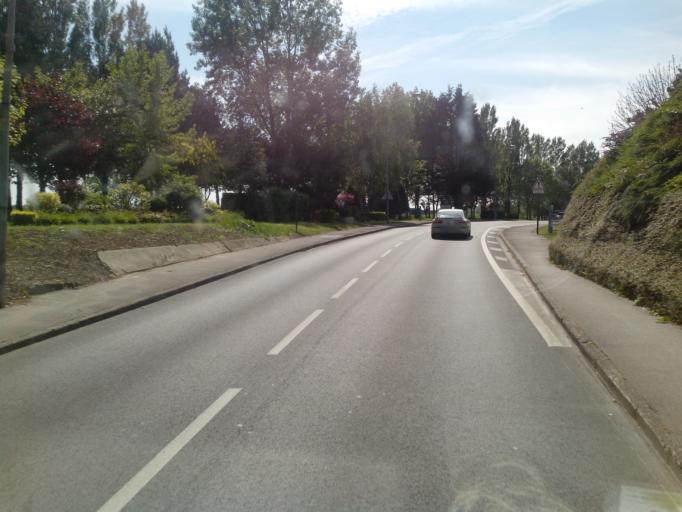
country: FR
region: Nord-Pas-de-Calais
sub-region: Departement du Pas-de-Calais
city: Etaples
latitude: 50.5111
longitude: 1.6442
